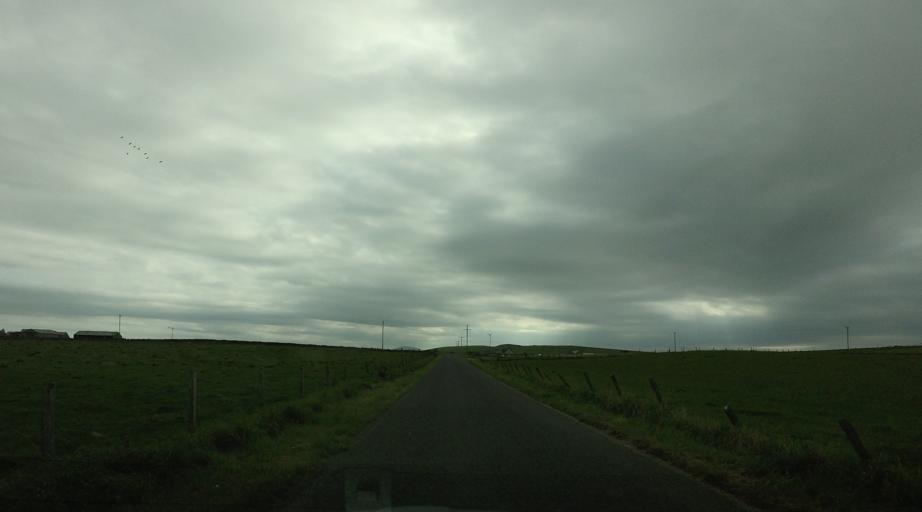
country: GB
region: Scotland
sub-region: Orkney Islands
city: Stromness
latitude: 59.0379
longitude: -3.3114
